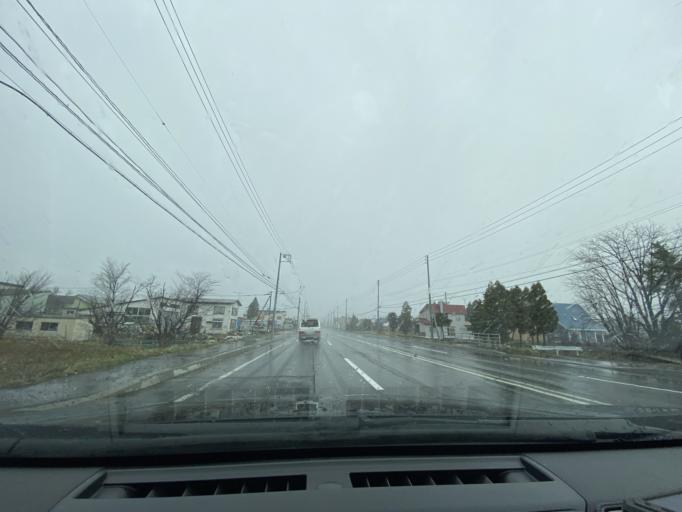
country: JP
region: Hokkaido
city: Takikawa
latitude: 43.6211
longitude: 141.9390
